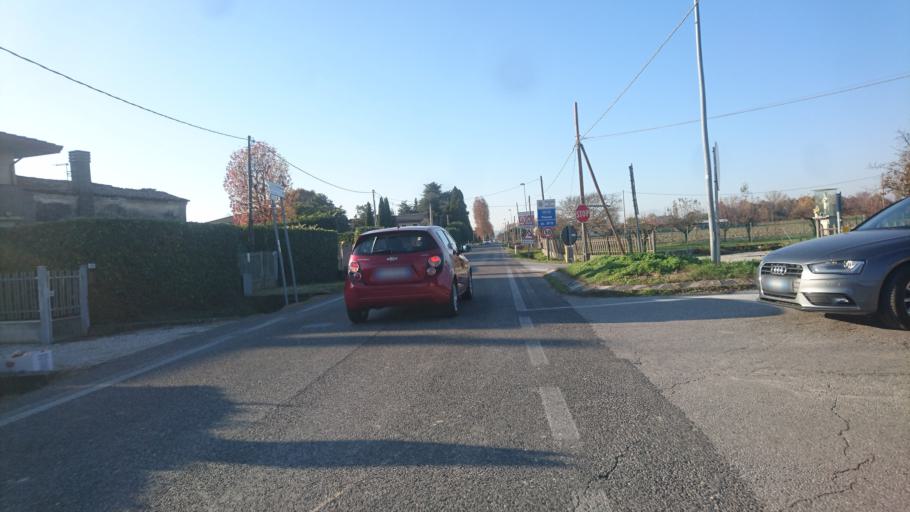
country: IT
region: Veneto
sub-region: Provincia di Padova
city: Mestrino
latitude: 45.4242
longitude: 11.7605
